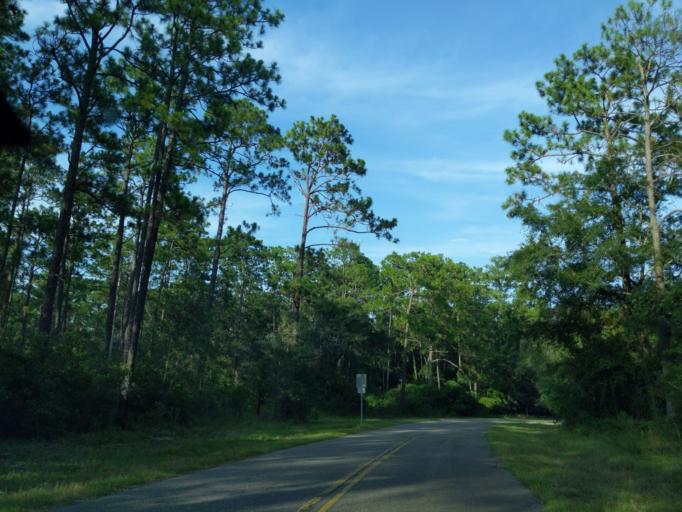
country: US
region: Florida
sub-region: Leon County
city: Tallahassee
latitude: 30.3449
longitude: -84.3856
